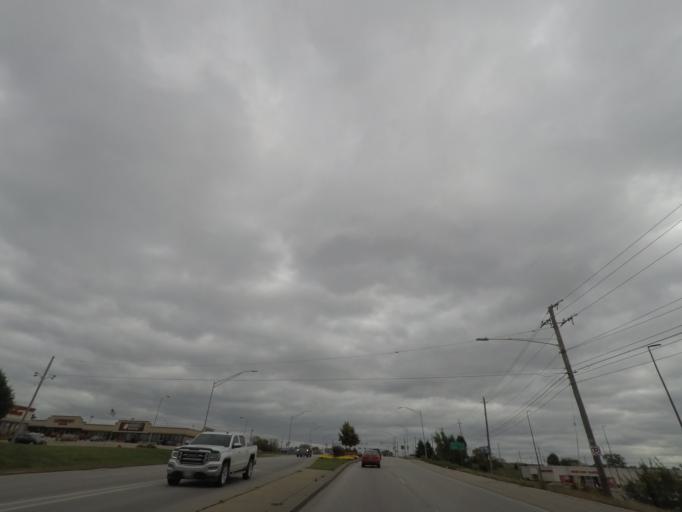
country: US
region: Iowa
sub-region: Polk County
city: Des Moines
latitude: 41.5263
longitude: -93.5999
